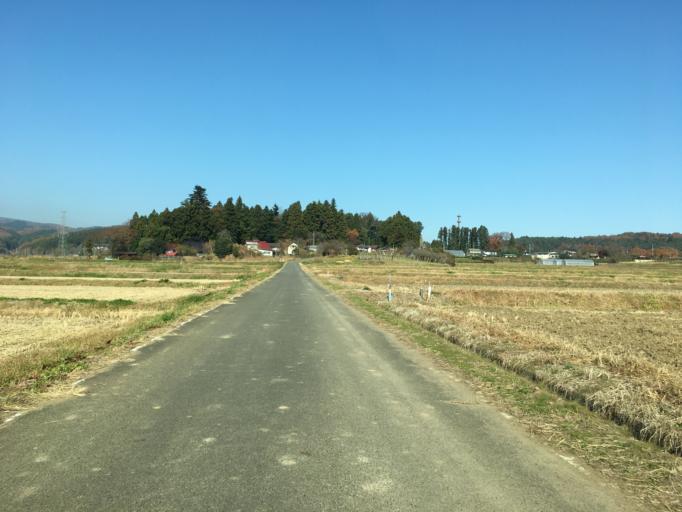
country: JP
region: Fukushima
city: Nihommatsu
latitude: 37.5765
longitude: 140.3903
